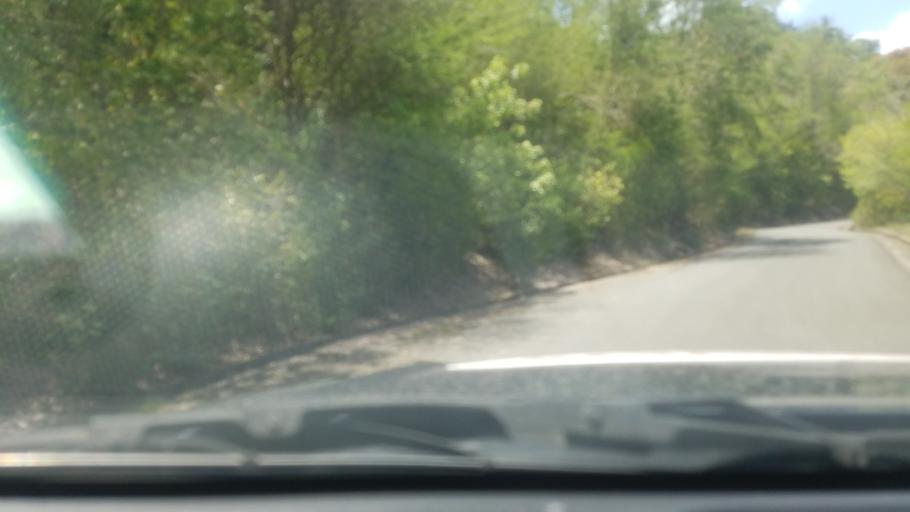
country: LC
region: Vieux-Fort
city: Vieux Fort
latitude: 13.7188
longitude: -60.9486
